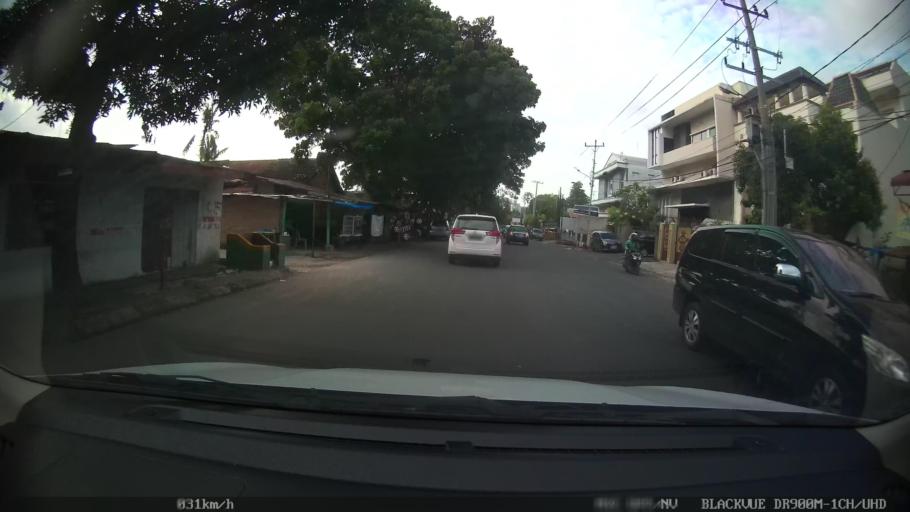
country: ID
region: North Sumatra
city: Medan
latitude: 3.5989
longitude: 98.6778
